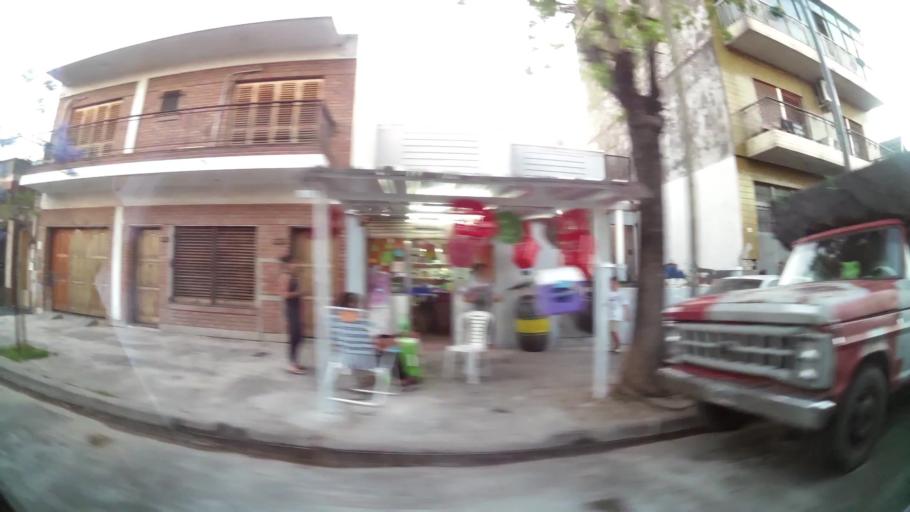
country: AR
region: Buenos Aires F.D.
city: Villa Lugano
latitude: -34.6667
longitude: -58.4691
